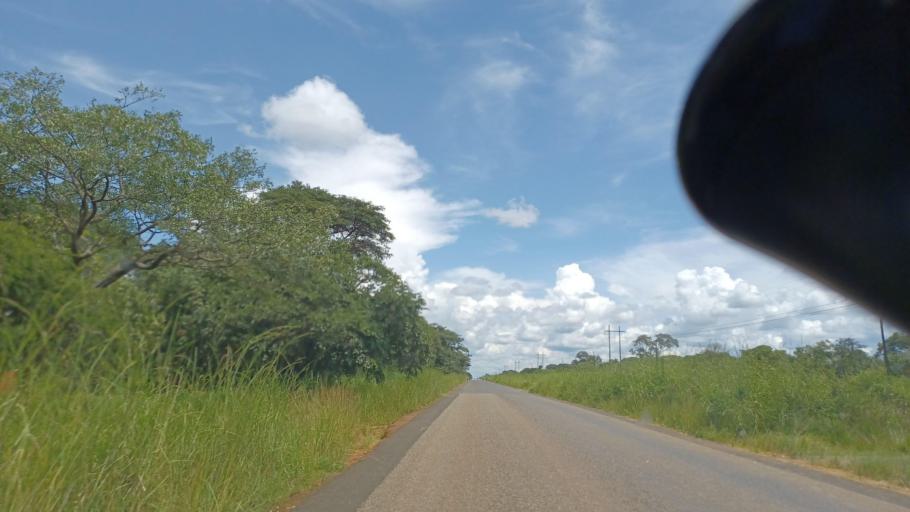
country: ZM
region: North-Western
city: Solwezi
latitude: -12.5610
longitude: 26.1412
